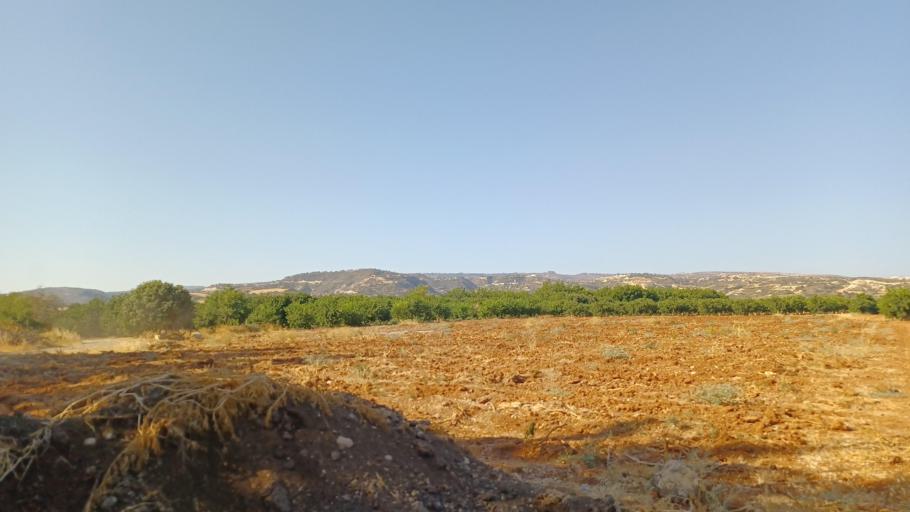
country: CY
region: Pafos
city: Polis
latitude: 35.0226
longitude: 32.4220
